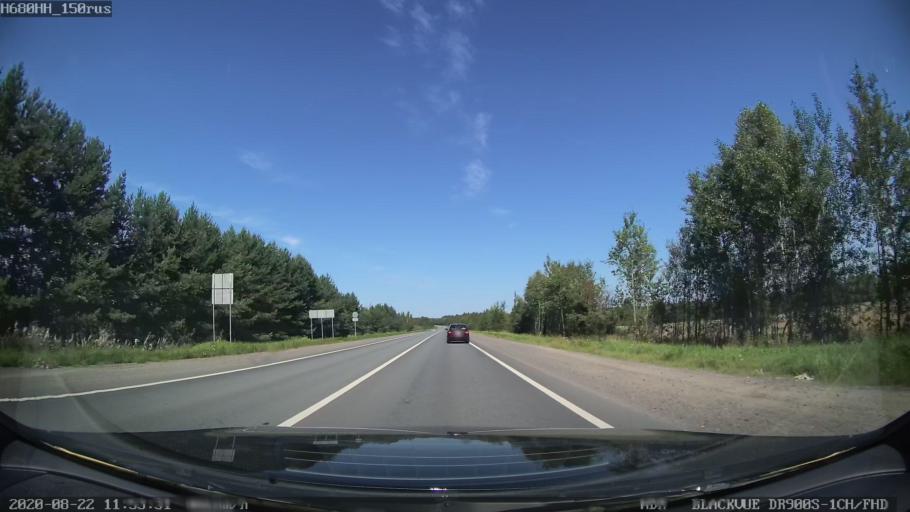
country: RU
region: Tverskaya
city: Vasil'yevskiy Mokh
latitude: 57.1280
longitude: 36.1107
